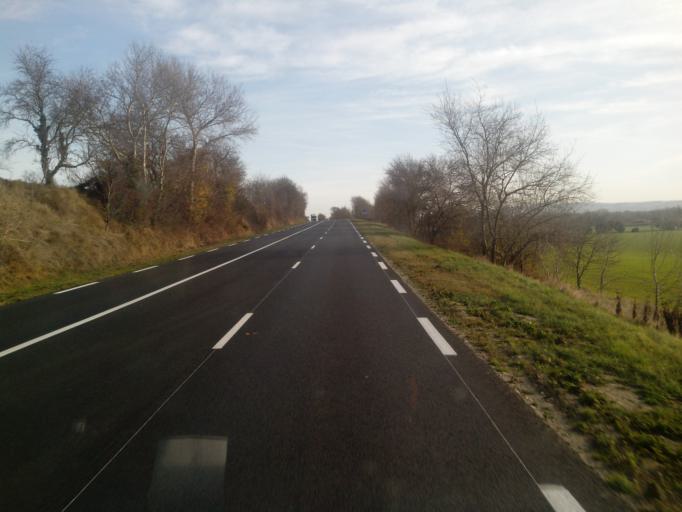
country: FR
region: Languedoc-Roussillon
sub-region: Departement de l'Aude
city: Bram
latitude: 43.2699
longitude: 2.1137
